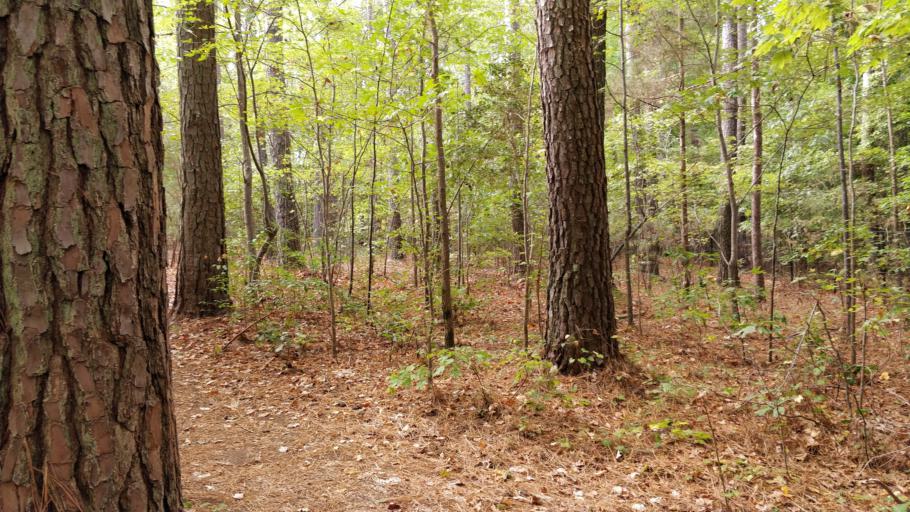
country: US
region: North Carolina
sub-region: Wake County
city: West Raleigh
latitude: 35.9064
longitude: -78.6709
